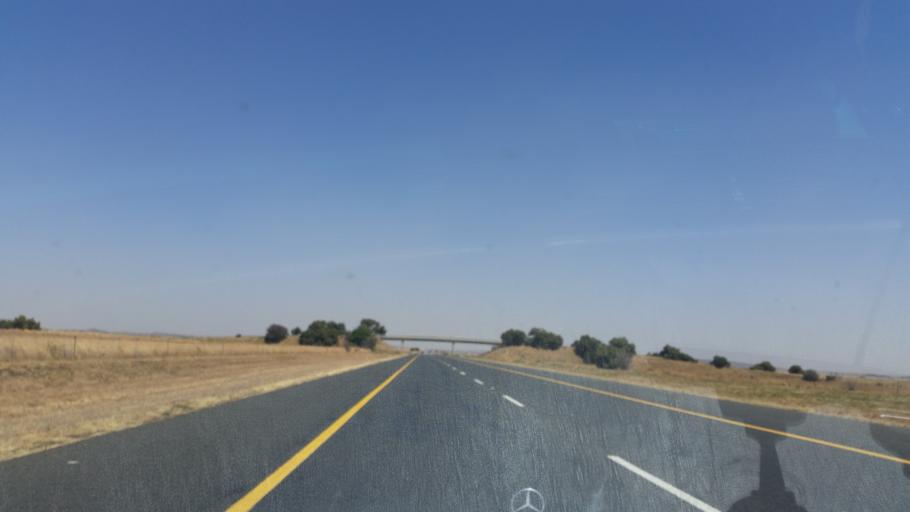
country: ZA
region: Orange Free State
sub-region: Lejweleputswa District Municipality
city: Winburg
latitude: -28.6523
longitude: 26.8730
